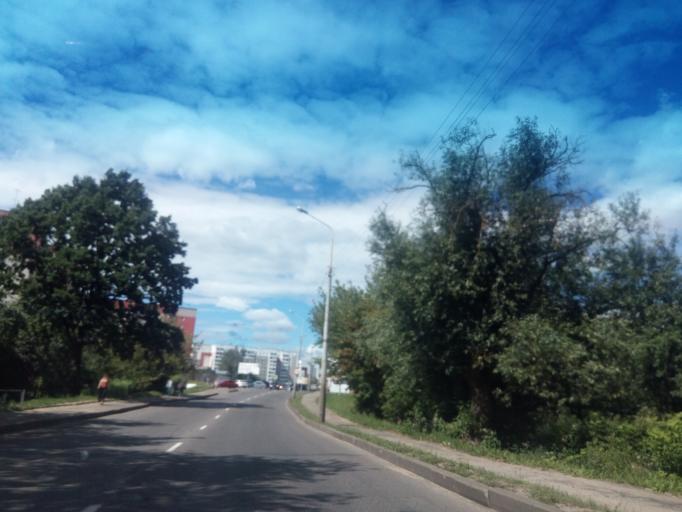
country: BY
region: Vitebsk
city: Polatsk
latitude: 55.4952
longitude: 28.7633
